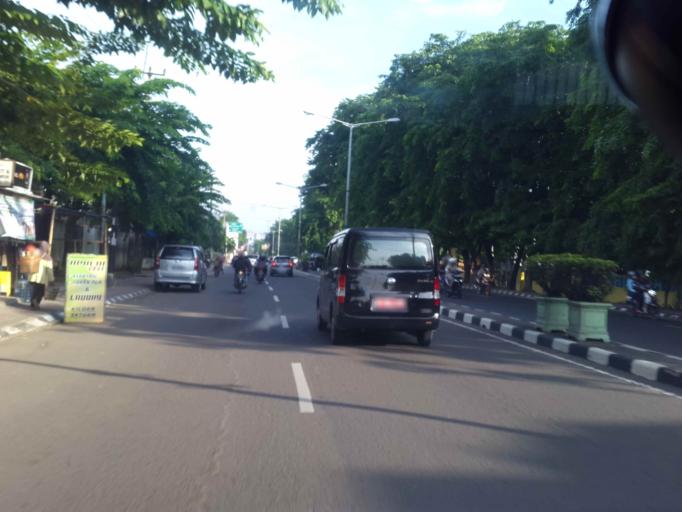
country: ID
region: West Java
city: Bekasi
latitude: -6.2495
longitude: 106.9980
